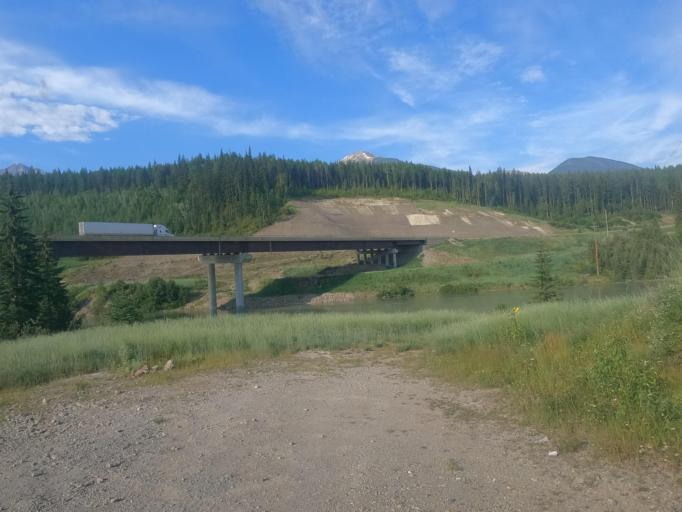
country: CA
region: British Columbia
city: Golden
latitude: 51.4854
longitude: -117.1805
